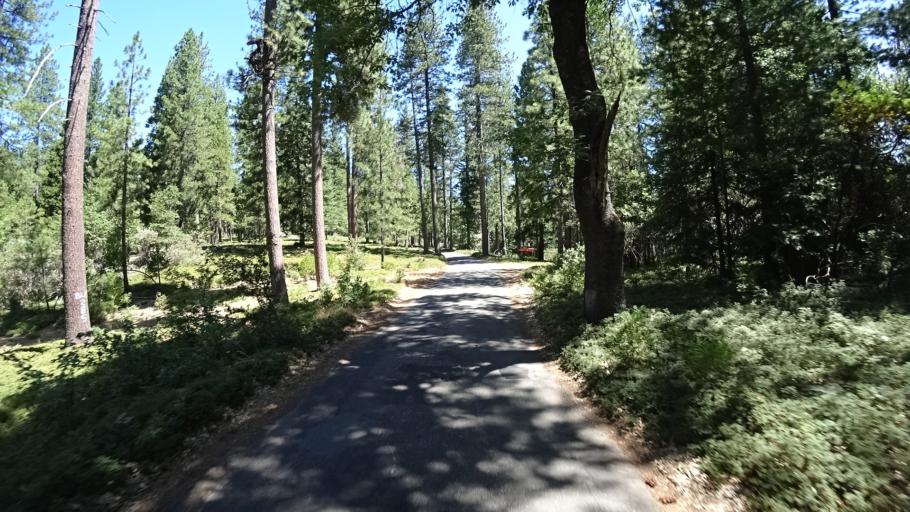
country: US
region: California
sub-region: Amador County
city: Pioneer
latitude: 38.4189
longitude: -120.4951
